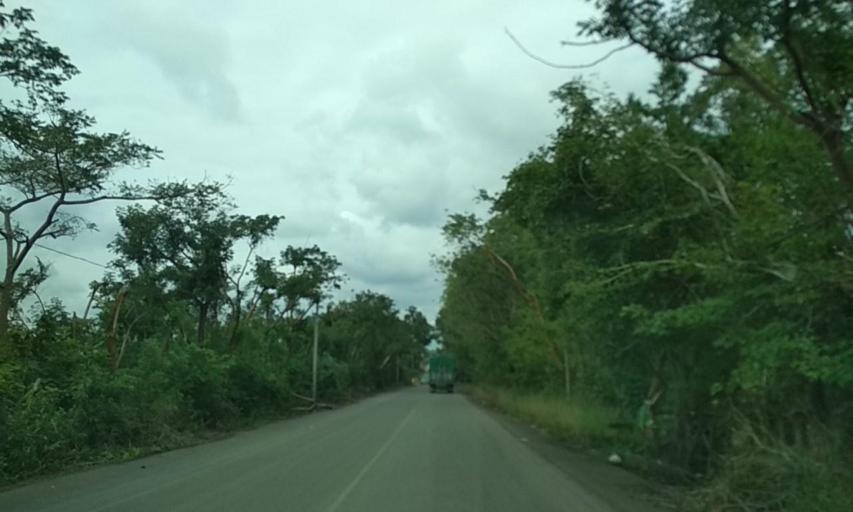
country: MX
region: Veracruz
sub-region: Papantla
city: El Chote
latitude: 20.3687
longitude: -97.3328
